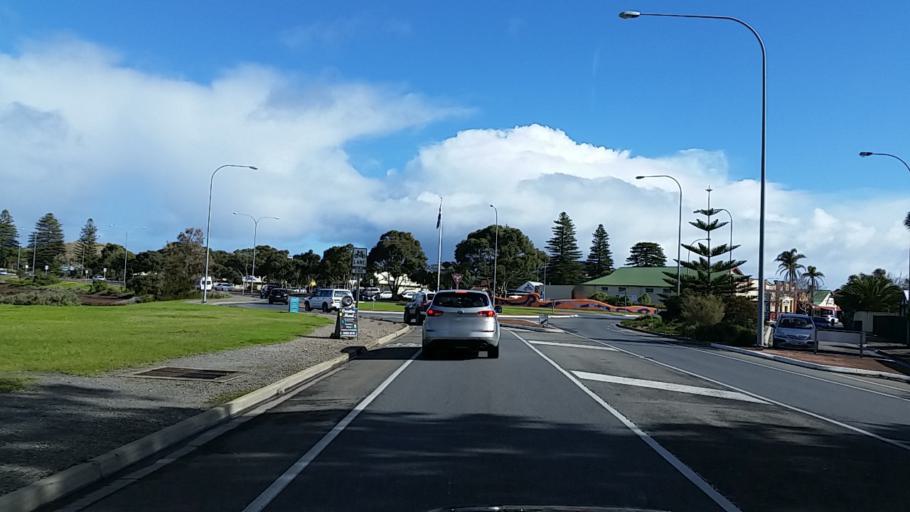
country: AU
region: South Australia
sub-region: Adelaide
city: Port Noarlunga
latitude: -35.1487
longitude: 138.4738
